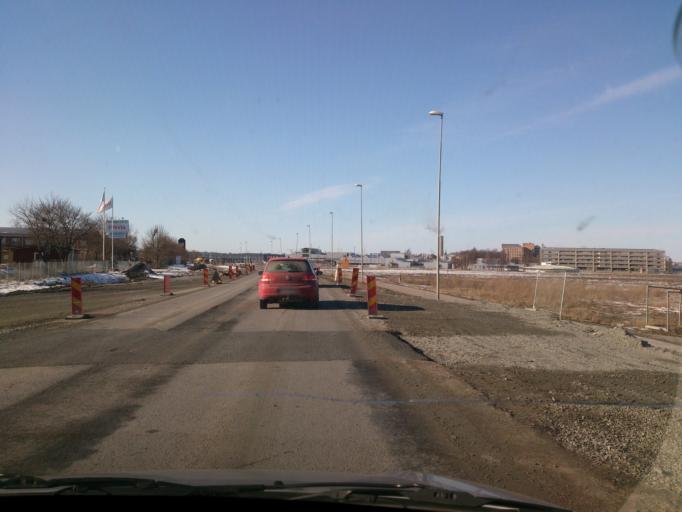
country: SE
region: Uppsala
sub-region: Uppsala Kommun
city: Saevja
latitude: 59.8465
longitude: 17.7186
